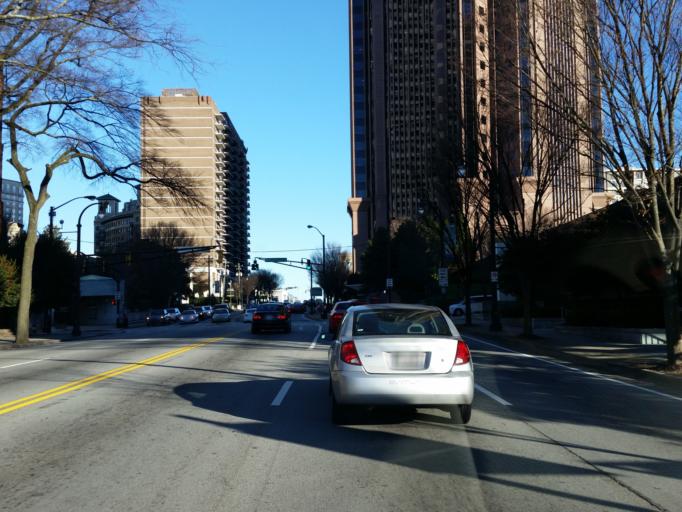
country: US
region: Georgia
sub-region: Fulton County
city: Atlanta
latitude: 33.7712
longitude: -84.3882
